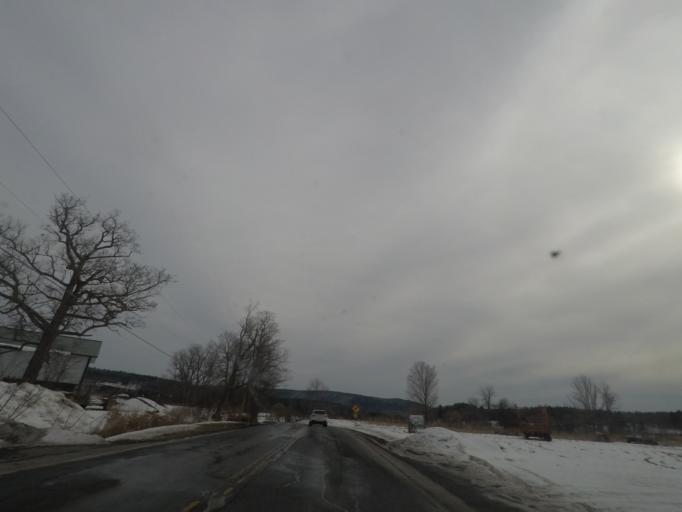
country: US
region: New York
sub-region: Albany County
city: Altamont
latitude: 42.6524
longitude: -74.1364
